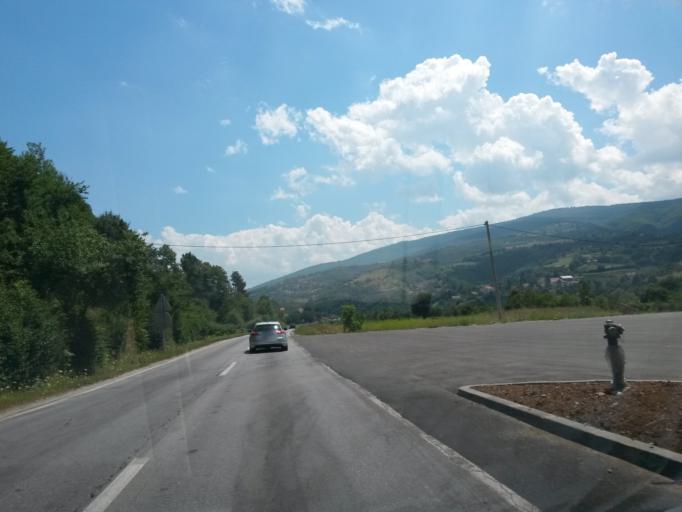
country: BA
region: Federation of Bosnia and Herzegovina
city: Turbe
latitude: 44.2393
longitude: 17.6053
